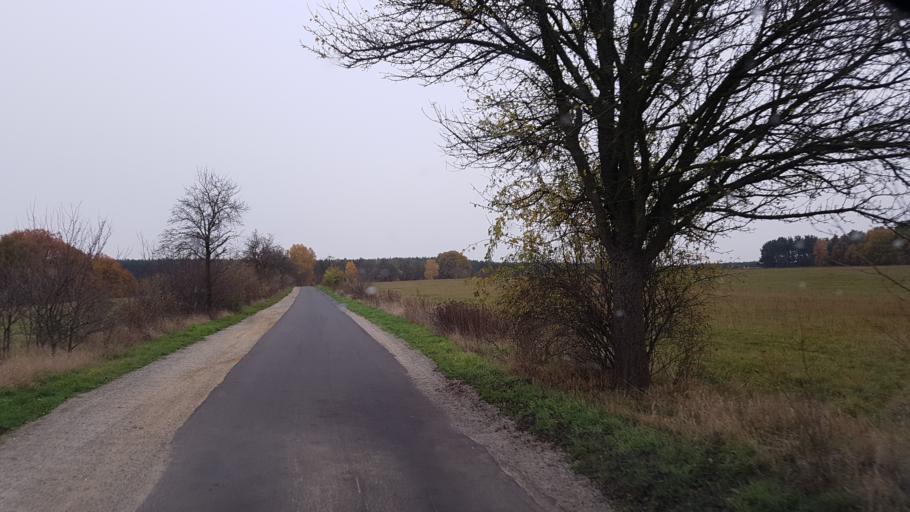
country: DE
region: Brandenburg
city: Crinitz
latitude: 51.7342
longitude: 13.7619
